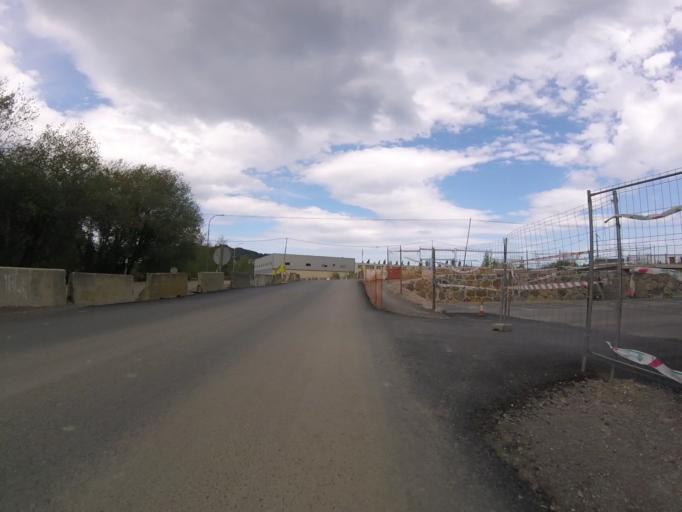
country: ES
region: Basque Country
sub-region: Provincia de Guipuzcoa
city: Zarautz
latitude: 43.2761
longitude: -2.1703
